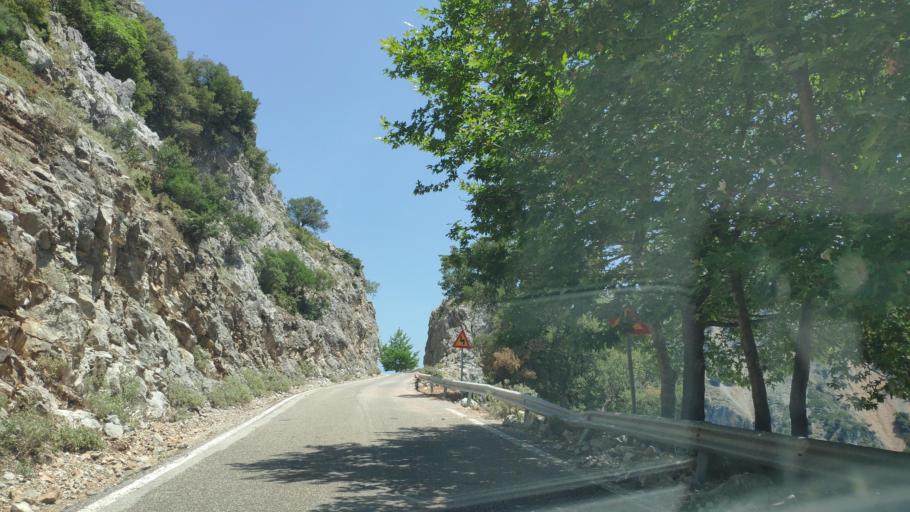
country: GR
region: West Greece
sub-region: Nomos Aitolias kai Akarnanias
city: Krikellos
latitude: 39.0120
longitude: 21.3724
